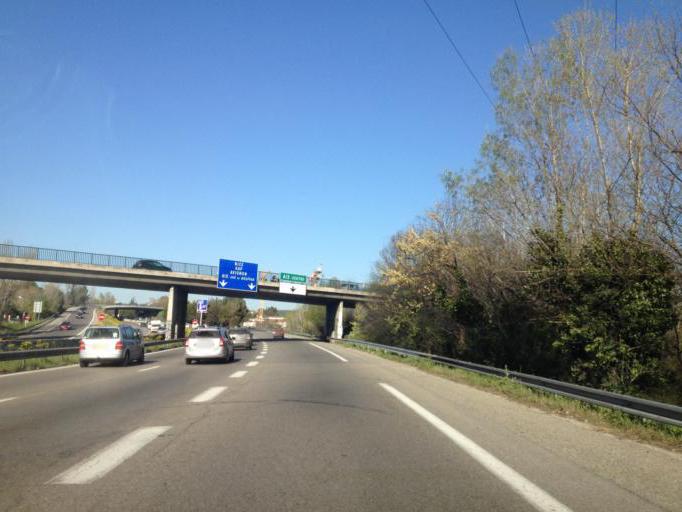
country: FR
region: Provence-Alpes-Cote d'Azur
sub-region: Departement des Bouches-du-Rhone
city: Aix-en-Provence
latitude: 43.5119
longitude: 5.4235
